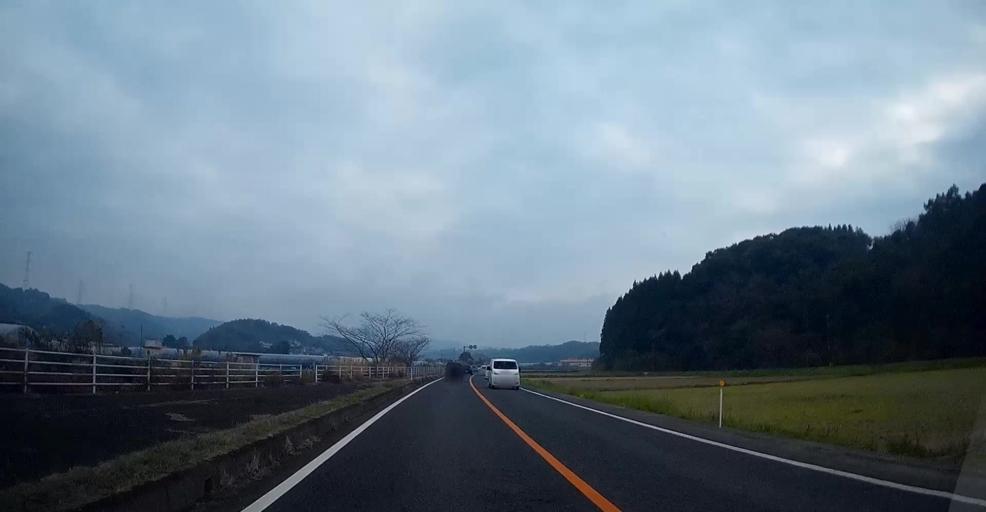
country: JP
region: Kumamoto
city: Yatsushiro
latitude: 32.6249
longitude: 130.5231
